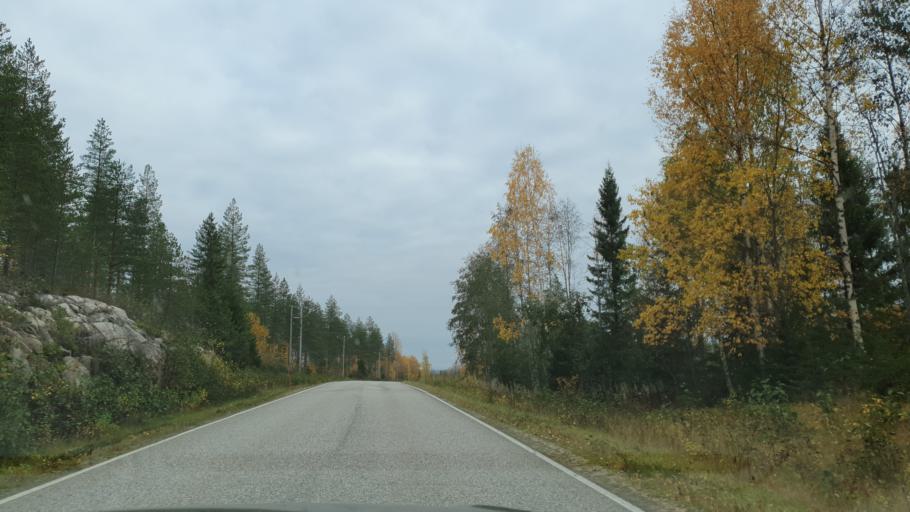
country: FI
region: Kainuu
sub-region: Kajaani
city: Ristijaervi
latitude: 64.4708
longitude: 28.2949
